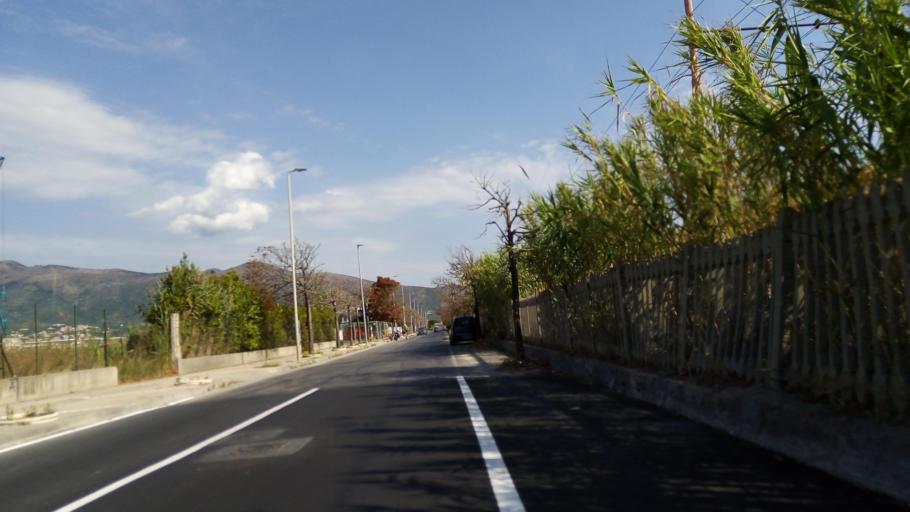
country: IT
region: Liguria
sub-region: Provincia di Savona
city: Albenga
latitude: 44.0671
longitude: 8.2250
